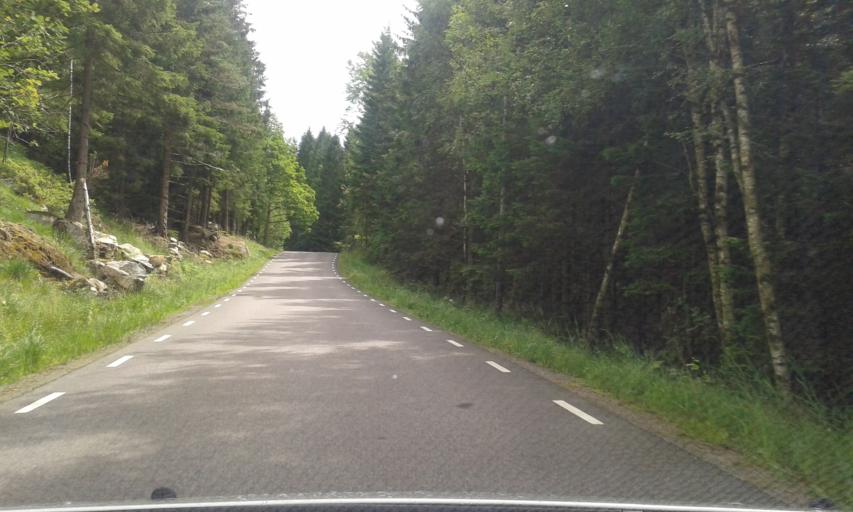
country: SE
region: Vaestra Goetaland
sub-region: Kungalvs Kommun
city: Diserod
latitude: 57.9644
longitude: 11.9992
